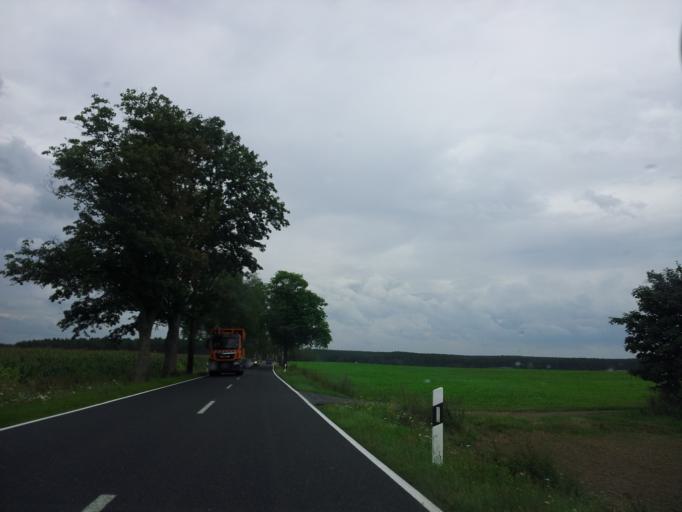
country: DE
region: Brandenburg
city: Gorzke
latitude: 52.1735
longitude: 12.3930
